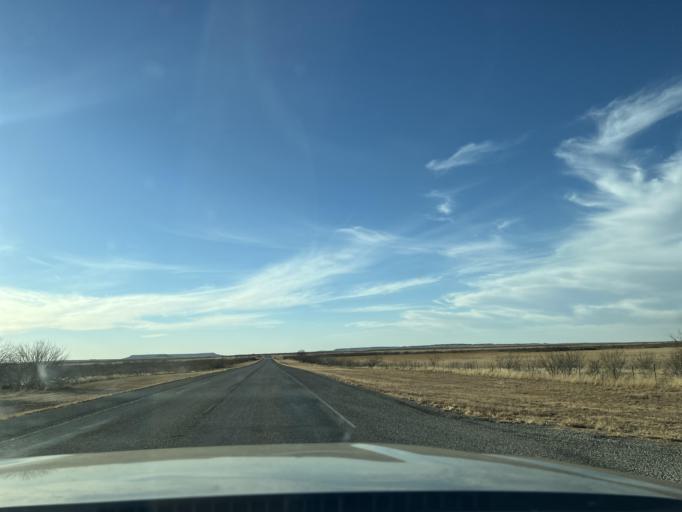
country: US
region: Texas
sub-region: Borden County
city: Gail
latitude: 32.7702
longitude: -101.3286
